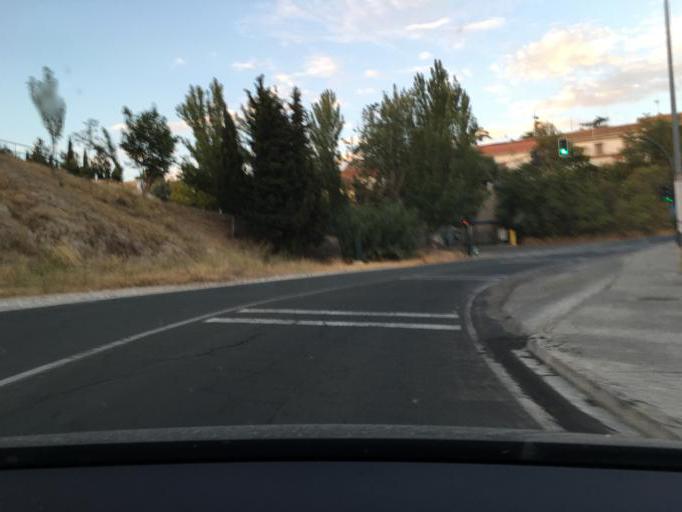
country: ES
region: Andalusia
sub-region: Provincia de Granada
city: Viznar
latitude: 37.2071
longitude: -3.5585
